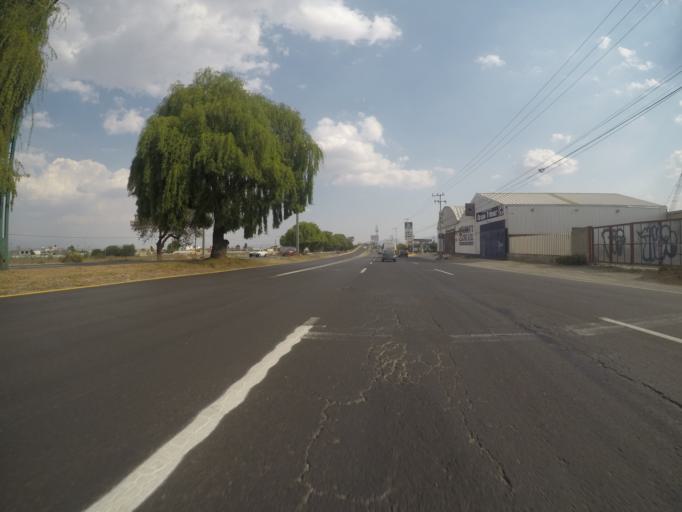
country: MX
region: Mexico
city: San Mateo Mexicaltzingo
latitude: 19.2192
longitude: -99.5920
